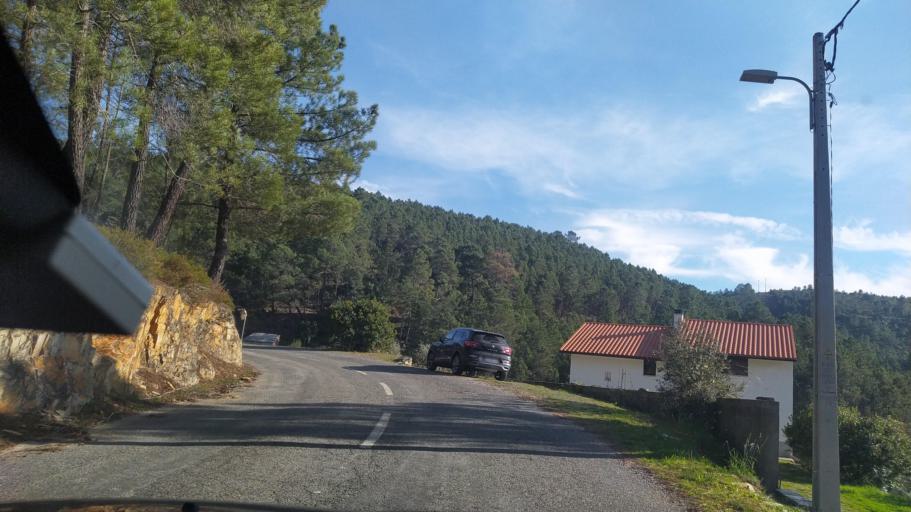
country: PT
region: Coimbra
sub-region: Oliveira do Hospital
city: Oliveira do Hospital
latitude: 40.2058
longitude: -7.7321
